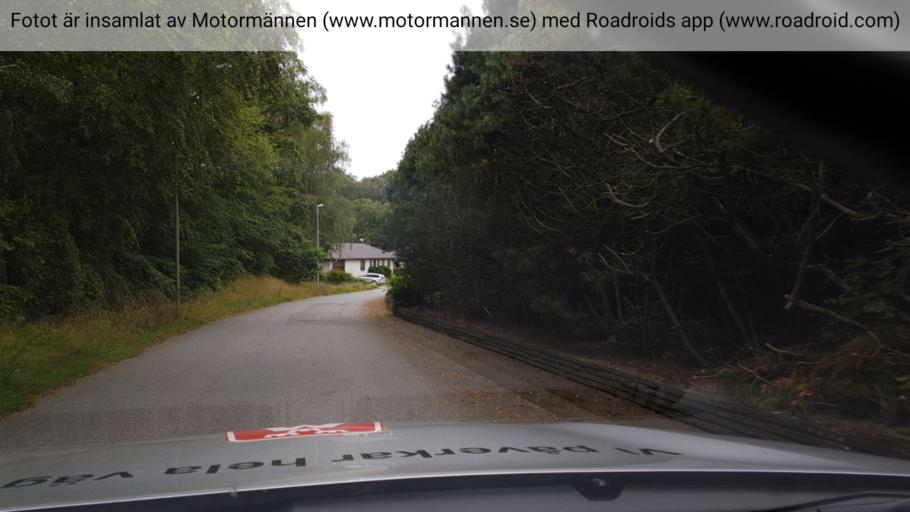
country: SE
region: Skane
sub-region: Hassleholms Kommun
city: Hassleholm
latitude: 56.1540
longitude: 13.7457
